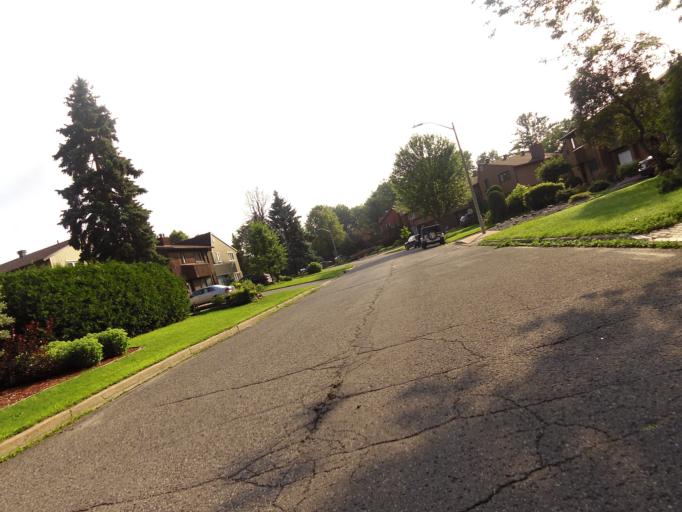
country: CA
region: Ontario
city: Ottawa
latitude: 45.3451
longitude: -75.6737
